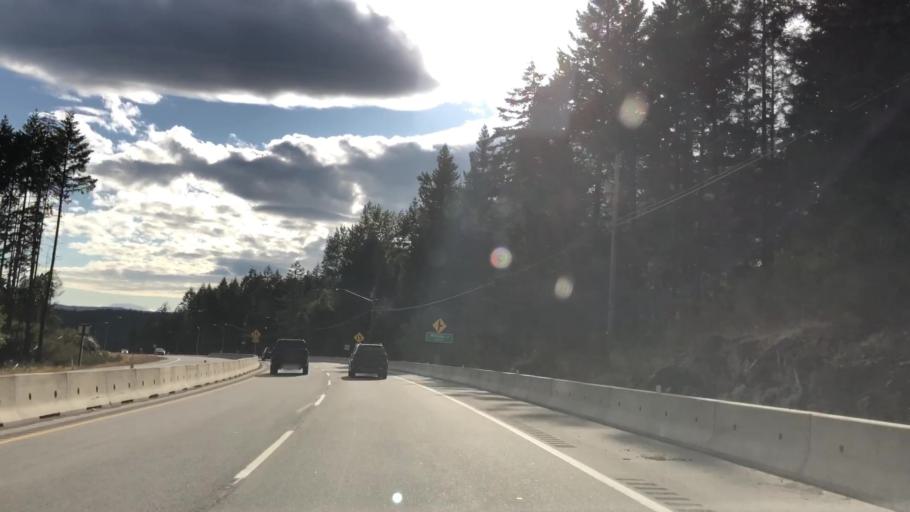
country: CA
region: British Columbia
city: Langford
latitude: 48.5677
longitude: -123.5589
